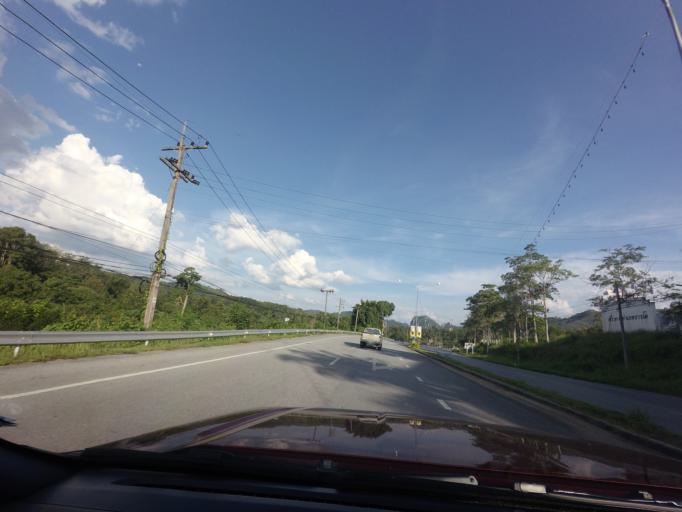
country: TH
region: Yala
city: Than To
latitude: 6.1689
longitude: 101.1806
